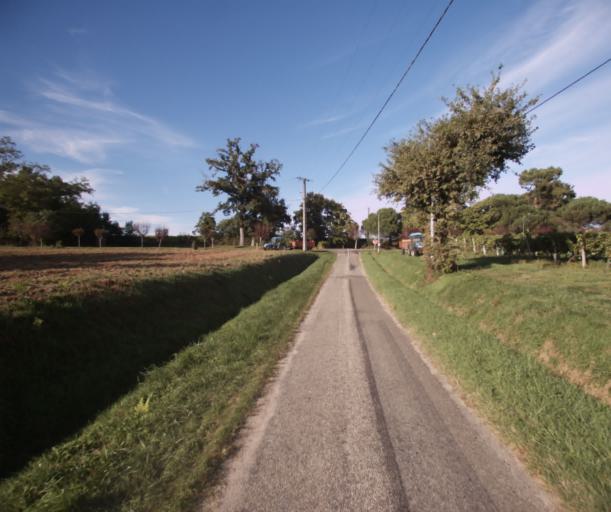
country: FR
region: Midi-Pyrenees
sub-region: Departement du Gers
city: Eauze
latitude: 43.8617
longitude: 0.0325
